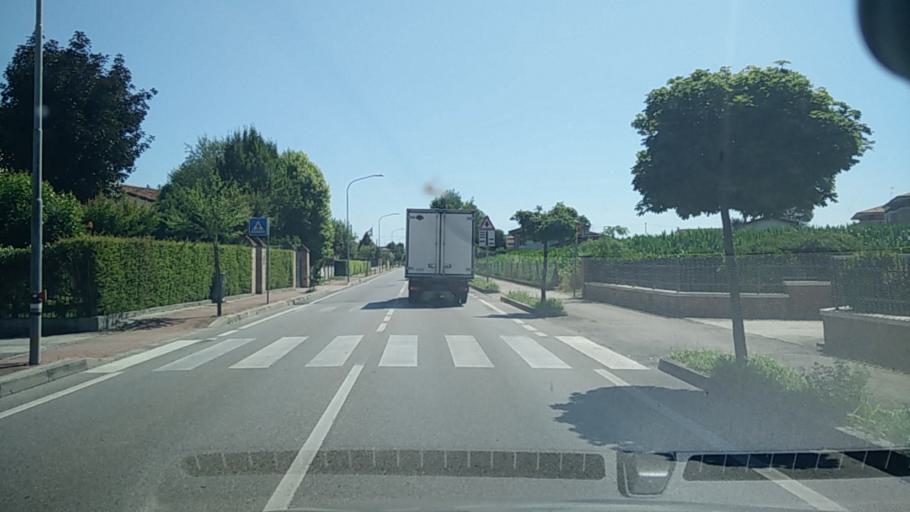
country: IT
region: Veneto
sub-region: Provincia di Venezia
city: Camponogara
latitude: 45.3837
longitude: 12.0864
